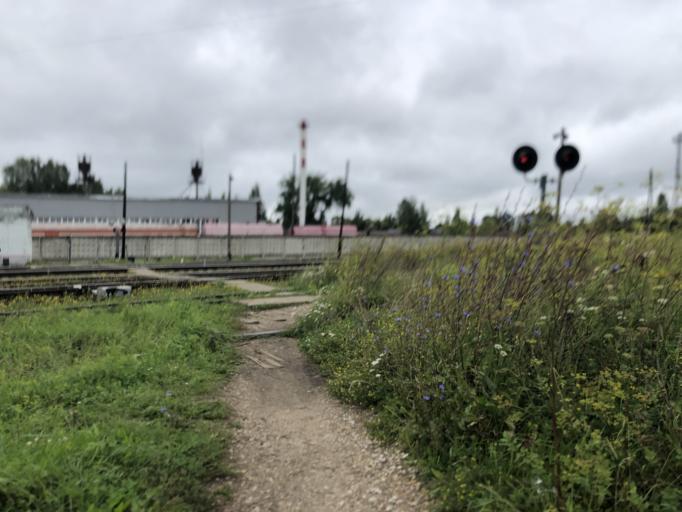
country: RU
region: Tverskaya
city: Rzhev
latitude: 56.2389
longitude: 34.3354
